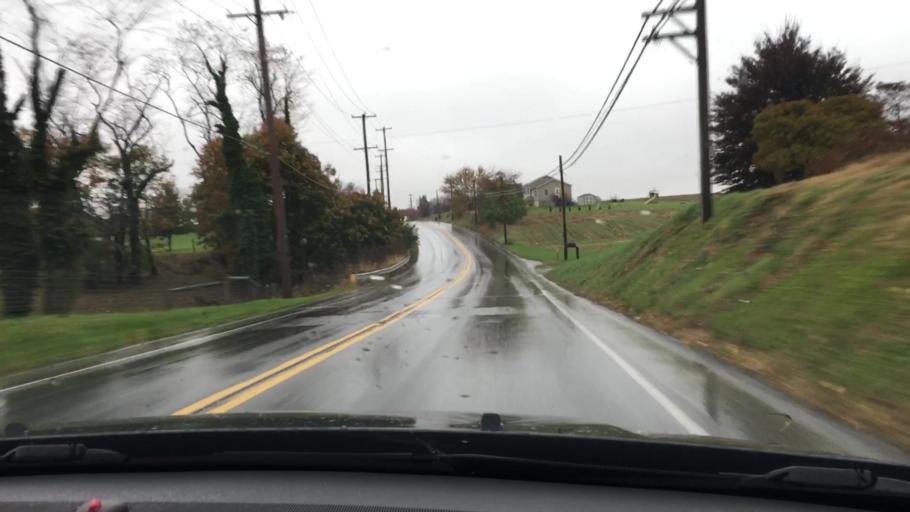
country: US
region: Pennsylvania
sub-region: York County
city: Susquehanna Trails
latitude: 39.8131
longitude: -76.3794
